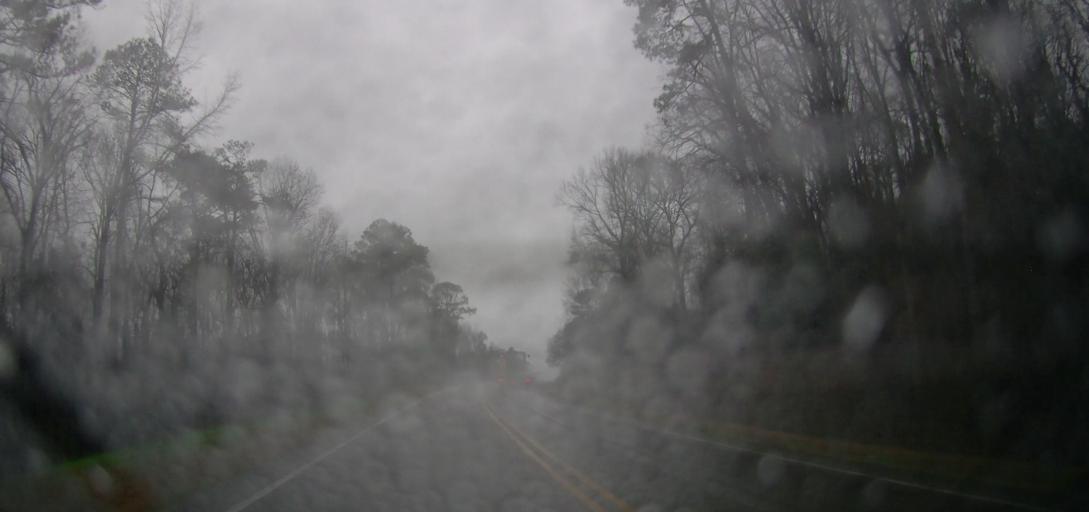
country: US
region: Alabama
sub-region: Autauga County
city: Prattville
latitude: 32.4898
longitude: -86.5445
